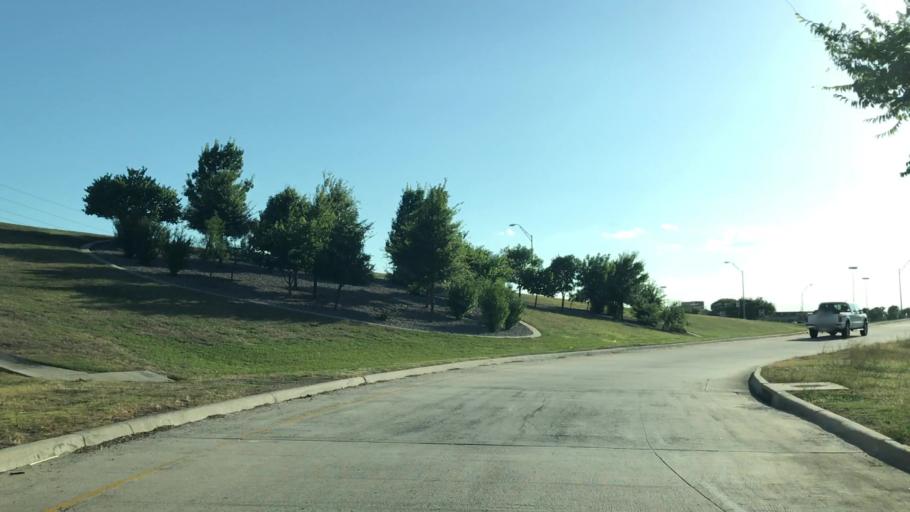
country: US
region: Texas
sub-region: Collin County
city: Plano
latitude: 33.0381
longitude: -96.7047
